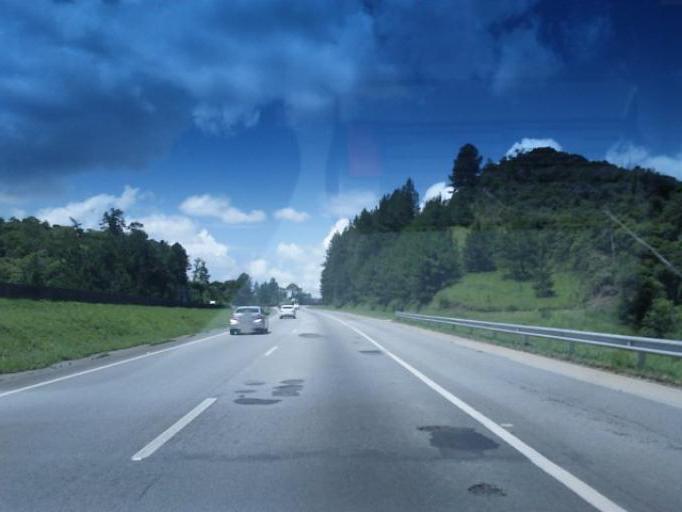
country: BR
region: Sao Paulo
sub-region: Juquitiba
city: Juquitiba
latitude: -23.9480
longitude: -47.0999
